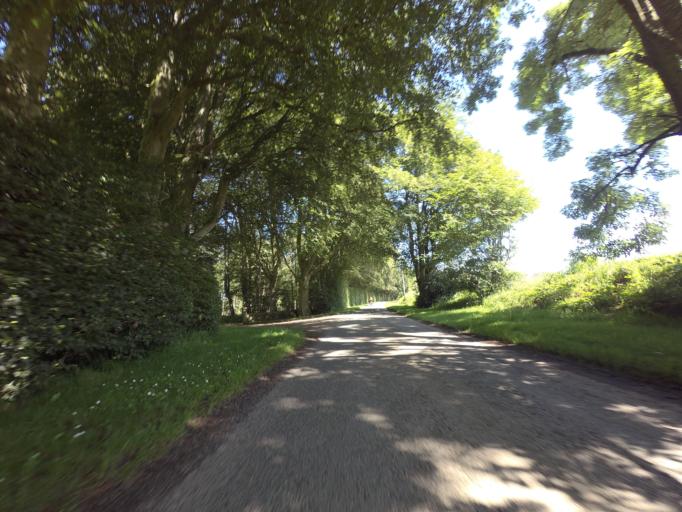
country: GB
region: Scotland
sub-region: Aberdeenshire
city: Macduff
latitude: 57.6270
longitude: -2.4933
